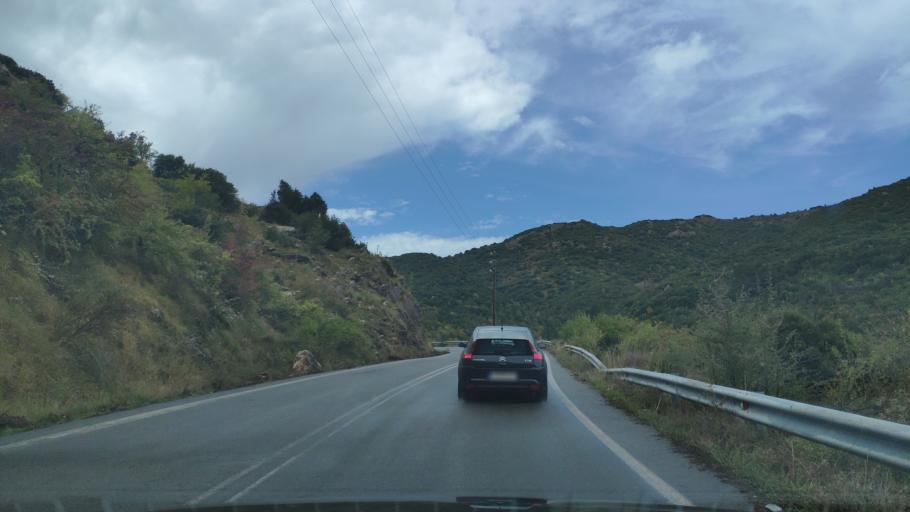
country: GR
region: Peloponnese
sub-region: Nomos Arkadias
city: Dimitsana
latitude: 37.6061
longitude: 22.0420
